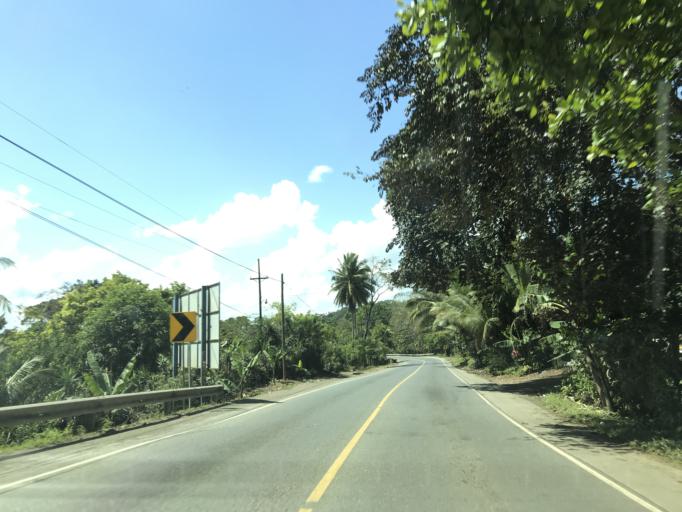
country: GT
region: Izabal
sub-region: Municipio de Puerto Barrios
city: Puerto Barrios
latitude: 15.6568
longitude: -88.5506
